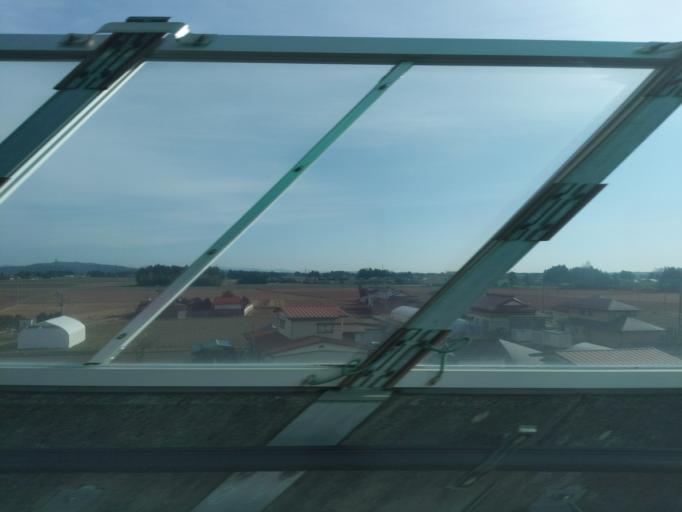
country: JP
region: Miyagi
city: Furukawa
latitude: 38.5982
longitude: 140.9812
